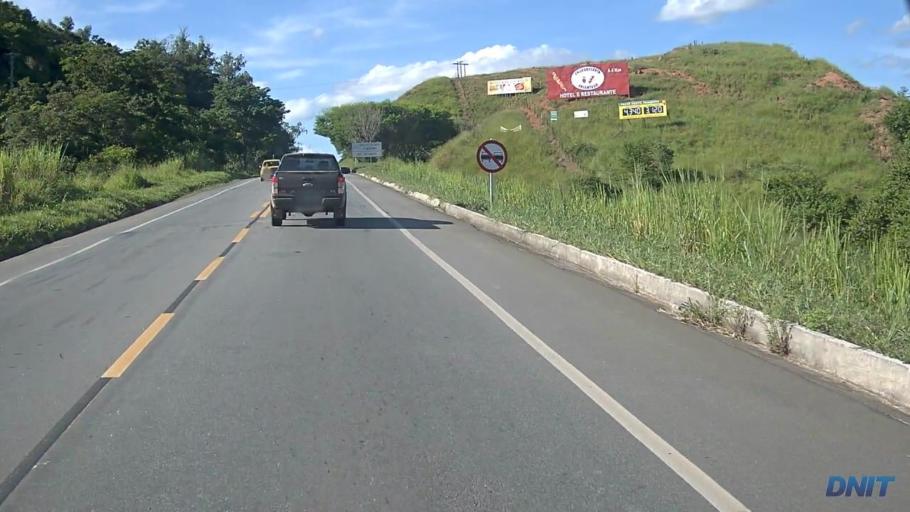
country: BR
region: Minas Gerais
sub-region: Belo Oriente
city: Belo Oriente
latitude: -19.2528
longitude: -42.3402
